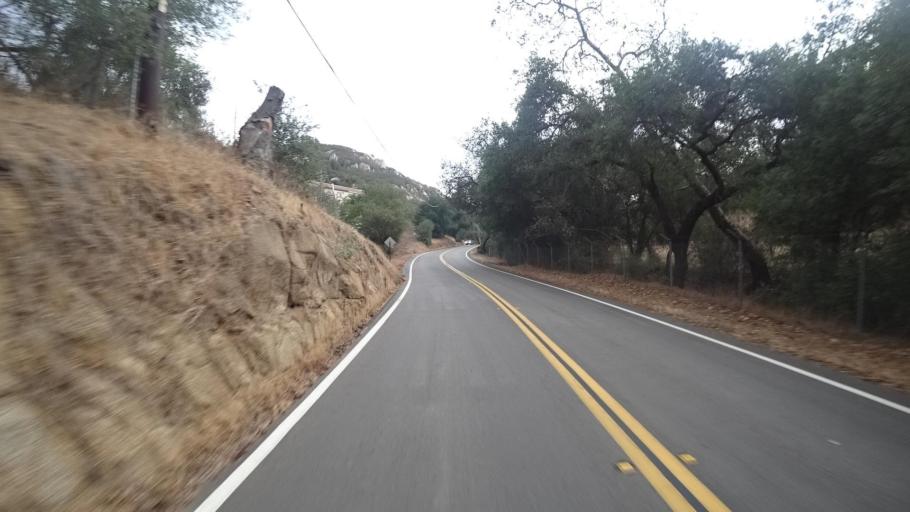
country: US
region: California
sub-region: San Diego County
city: San Pasqual
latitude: 33.0527
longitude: -116.9702
